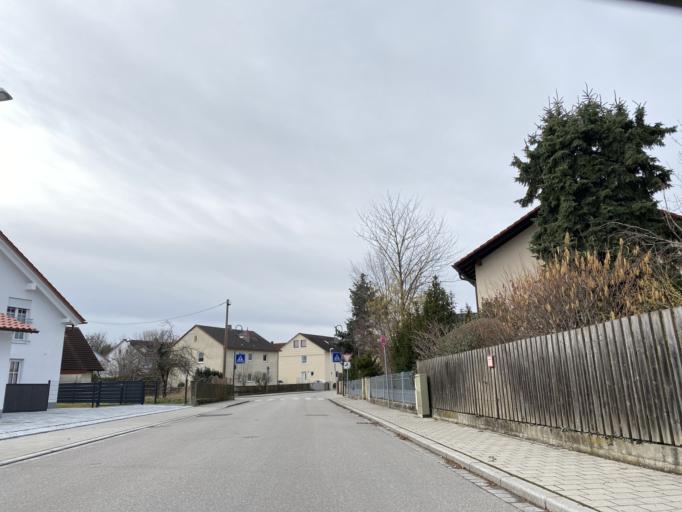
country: DE
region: Bavaria
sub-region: Upper Bavaria
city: Emmering
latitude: 48.1845
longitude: 11.2729
